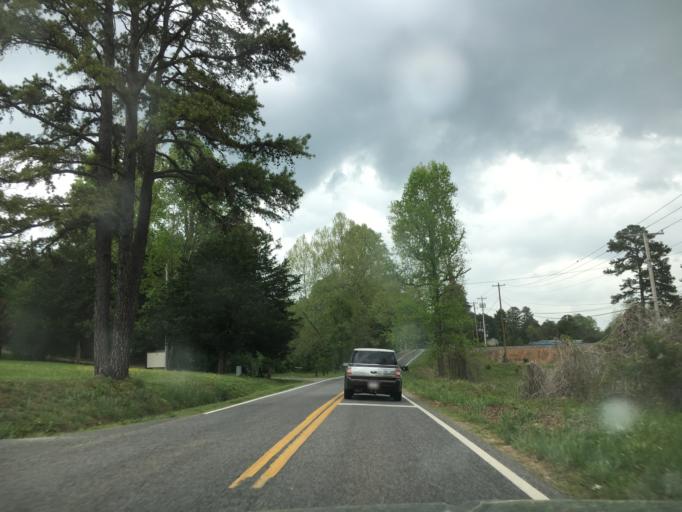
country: US
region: Virginia
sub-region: Campbell County
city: Rustburg
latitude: 37.3310
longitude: -79.1138
